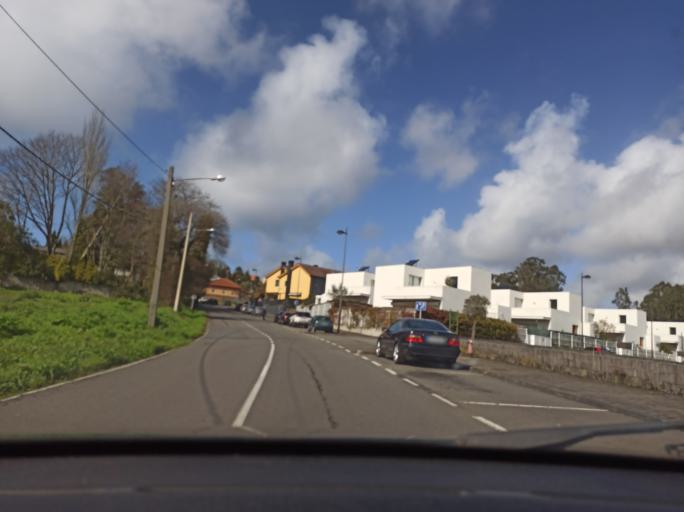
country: ES
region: Galicia
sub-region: Provincia da Coruna
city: Cambre
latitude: 43.3228
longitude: -8.3526
